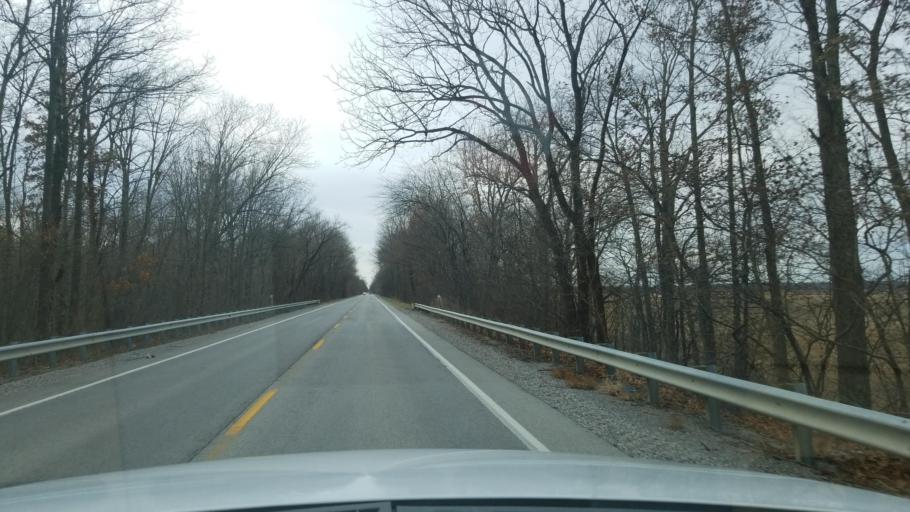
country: US
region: Illinois
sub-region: White County
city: Carmi
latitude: 37.9336
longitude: -88.0851
